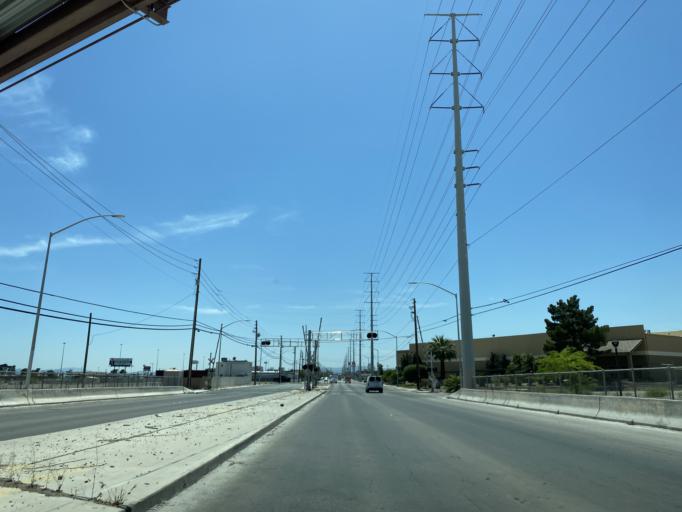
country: US
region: Nevada
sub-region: Clark County
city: North Las Vegas
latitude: 36.2273
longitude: -115.1203
